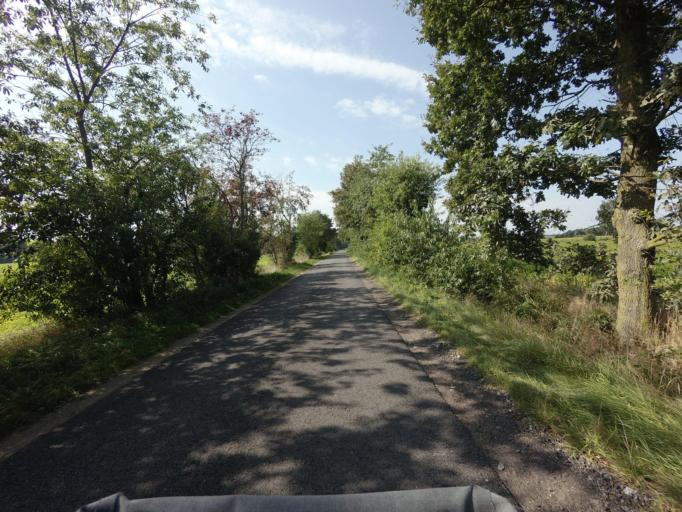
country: DE
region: Lower Saxony
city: Itterbeck
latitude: 52.5306
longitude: 6.8060
